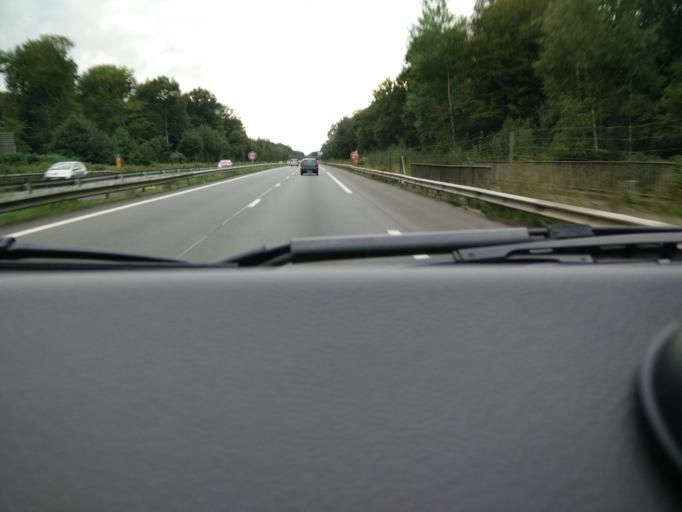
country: FR
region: Nord-Pas-de-Calais
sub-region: Departement du Nord
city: Saint-Amand-les-Eaux
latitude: 50.4114
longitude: 3.4292
